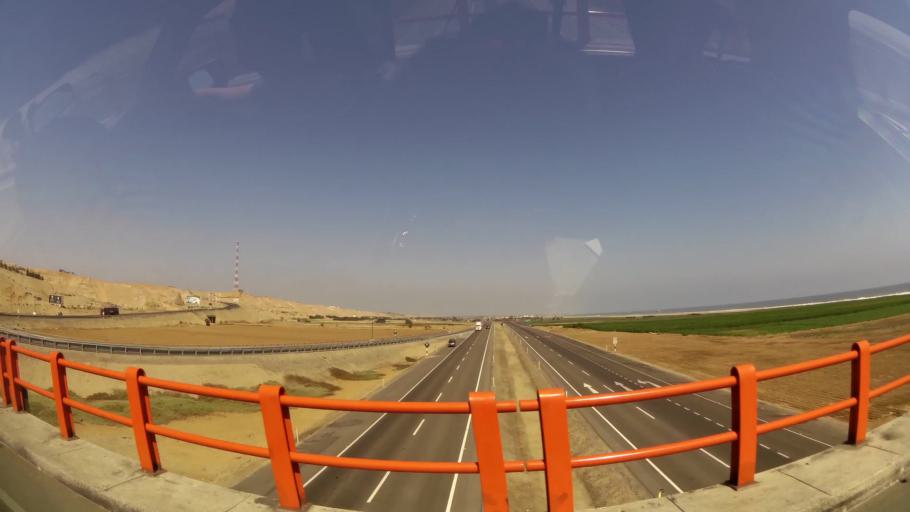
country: PE
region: Ica
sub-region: Provincia de Chincha
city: Sunampe
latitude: -13.4100
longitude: -76.1918
